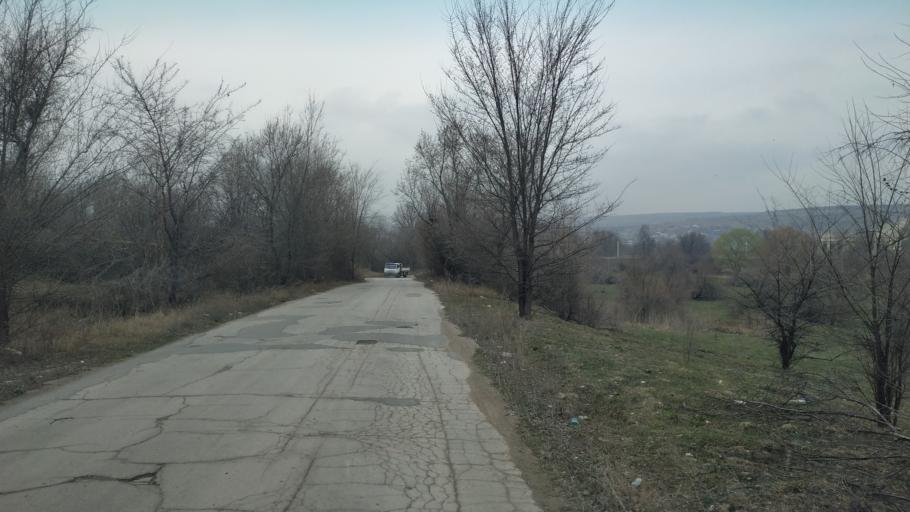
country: MD
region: Chisinau
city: Singera
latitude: 46.9230
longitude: 29.0045
